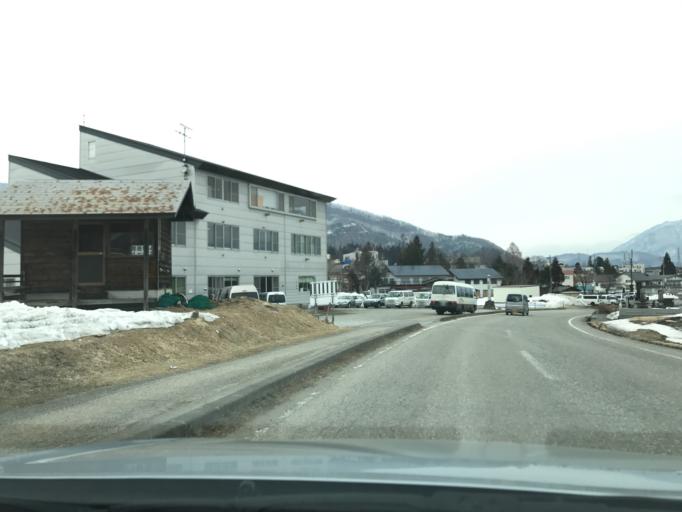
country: JP
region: Nagano
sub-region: Kitaazumi Gun
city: Hakuba
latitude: 36.6984
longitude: 137.8401
